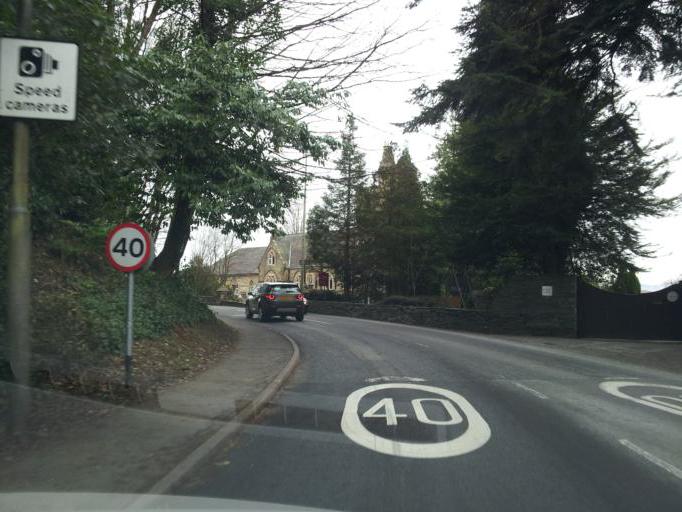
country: GB
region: England
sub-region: Cumbria
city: Windermere
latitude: 54.3859
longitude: -2.9156
